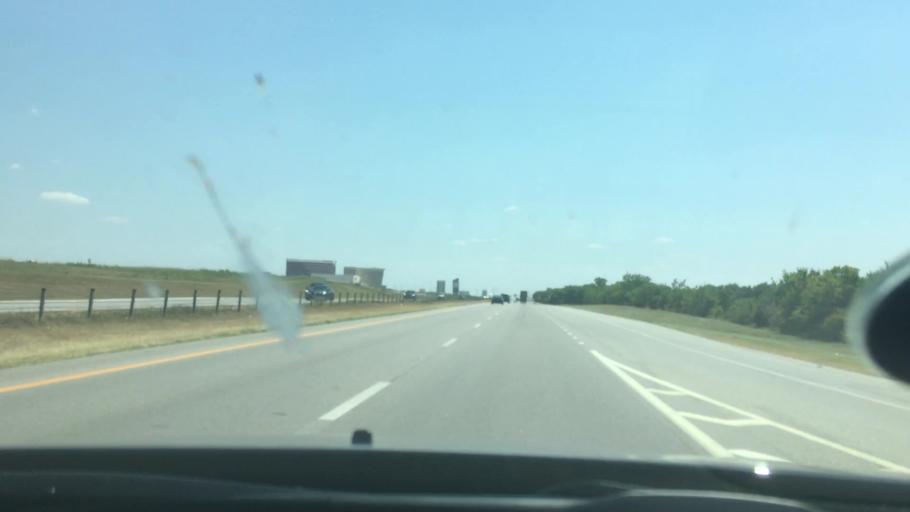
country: US
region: Oklahoma
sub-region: Bryan County
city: Calera
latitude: 33.9659
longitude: -96.4168
